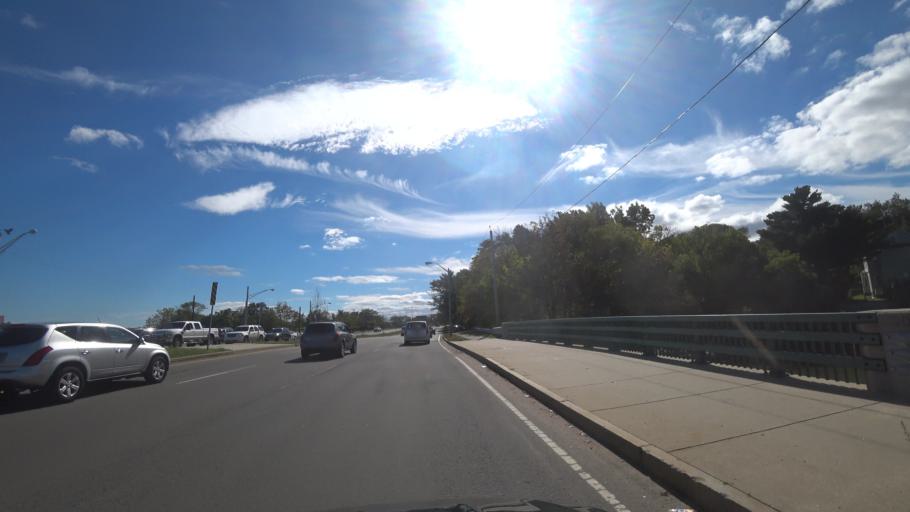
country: US
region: Massachusetts
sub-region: Suffolk County
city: South Boston
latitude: 42.3134
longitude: -71.0471
